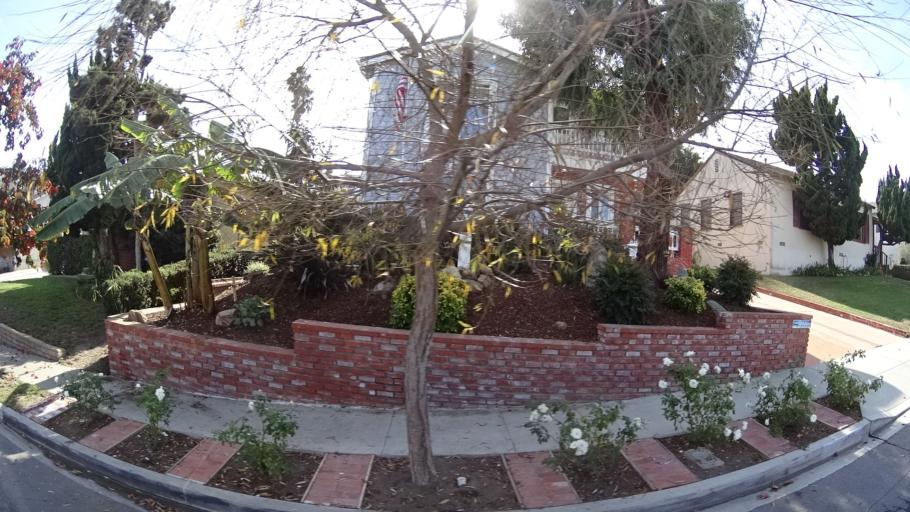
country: US
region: California
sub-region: Los Angeles County
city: Manhattan Beach
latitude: 33.8919
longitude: -118.3893
